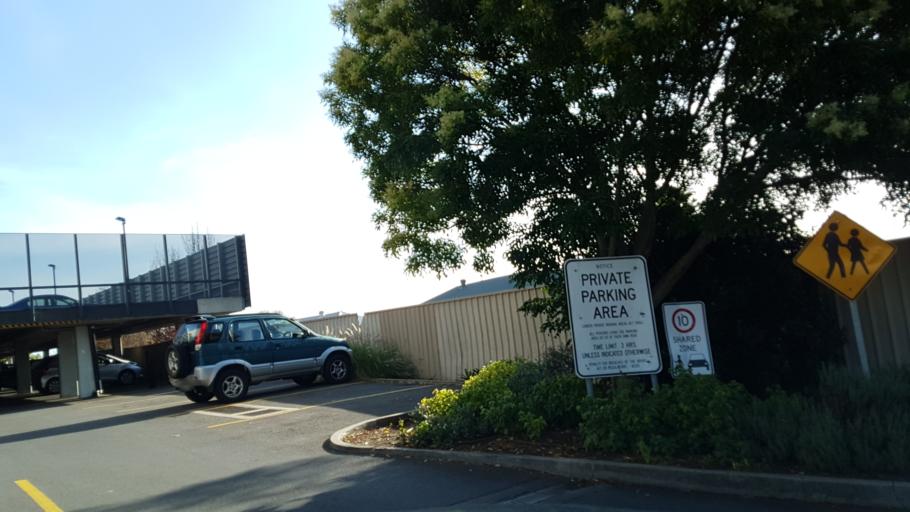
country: AU
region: South Australia
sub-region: Norwood Payneham St Peters
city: Marden
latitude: -34.8944
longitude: 138.6390
